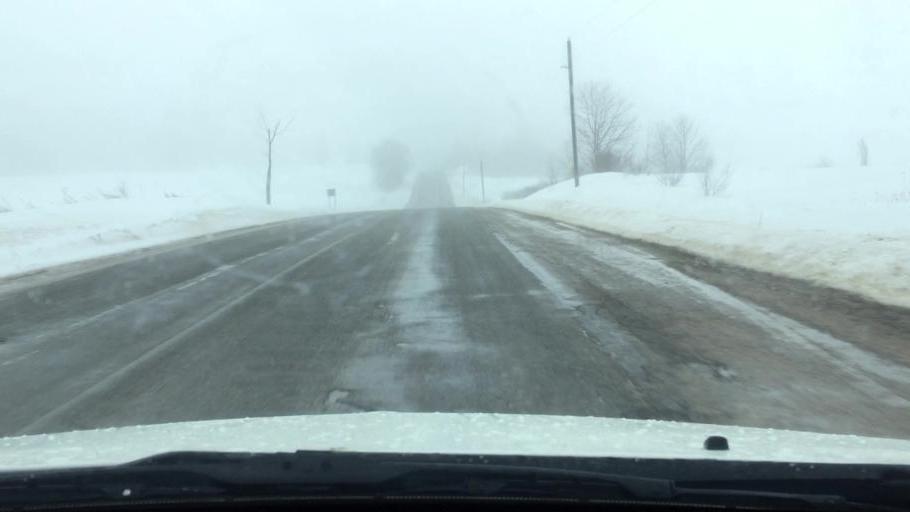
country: US
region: Michigan
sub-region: Charlevoix County
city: East Jordan
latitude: 45.1325
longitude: -85.1606
